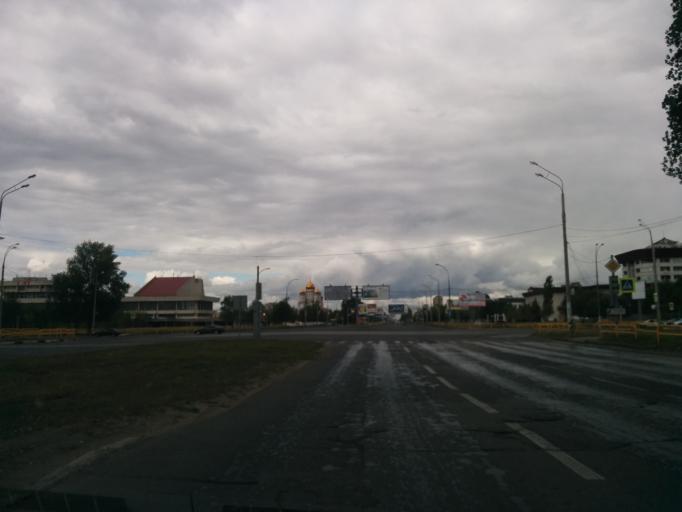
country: RU
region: Samara
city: Tol'yatti
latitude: 53.5142
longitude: 49.2782
